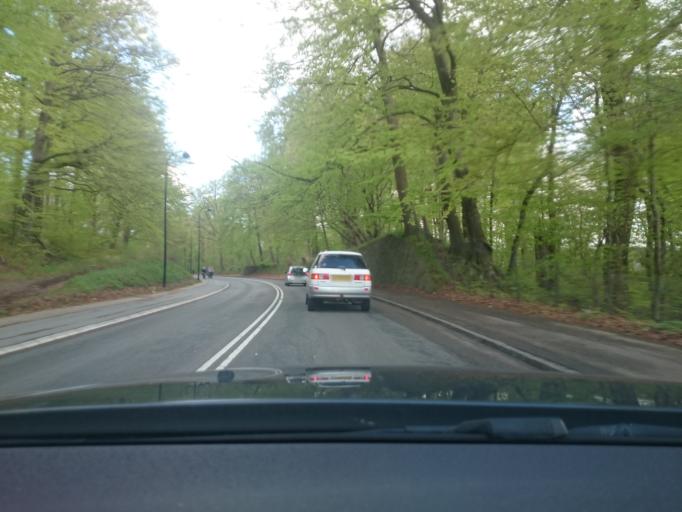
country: DK
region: Capital Region
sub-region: Gentofte Kommune
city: Charlottenlund
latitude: 55.7705
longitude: 12.5573
